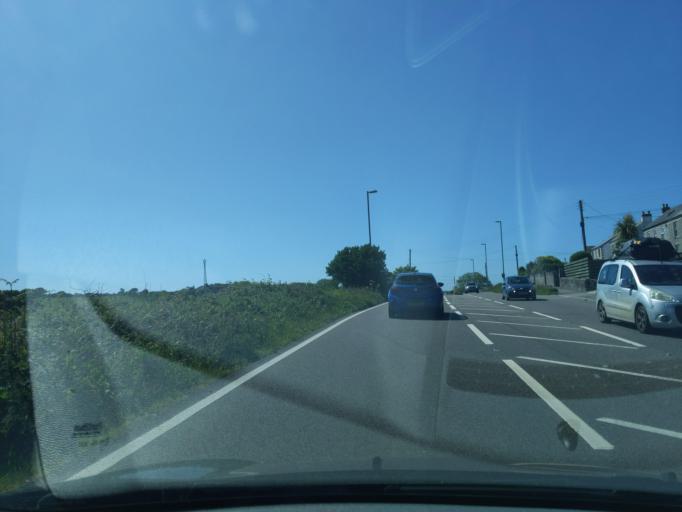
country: GB
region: England
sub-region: Cornwall
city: Penryn
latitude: 50.1644
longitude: -5.1612
